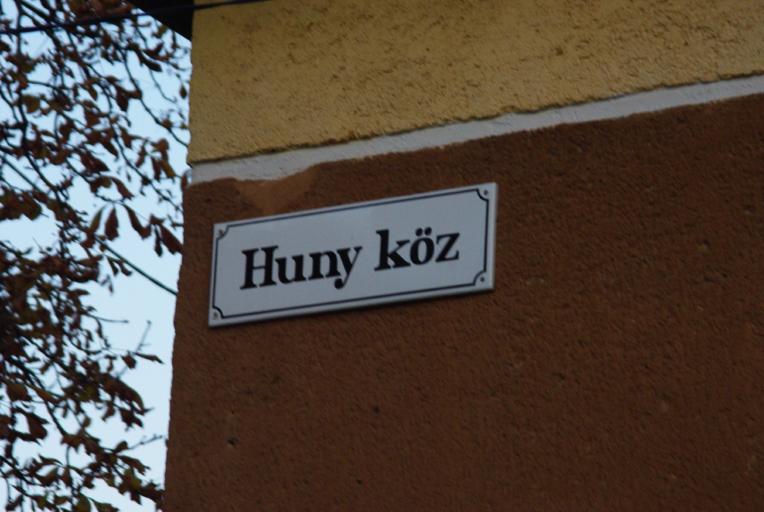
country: HU
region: Pest
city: Pilisszentivan
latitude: 47.6143
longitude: 18.8967
